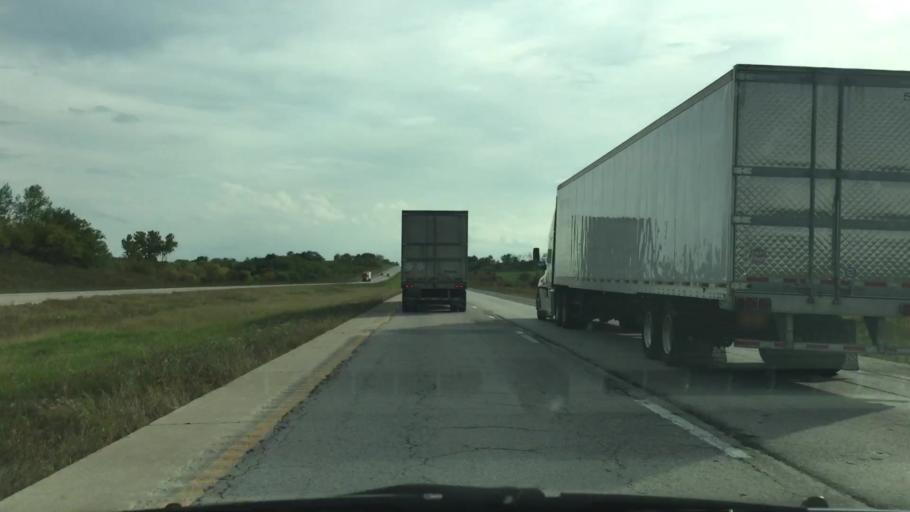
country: US
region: Iowa
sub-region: Decatur County
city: Lamoni
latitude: 40.5584
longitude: -93.9512
